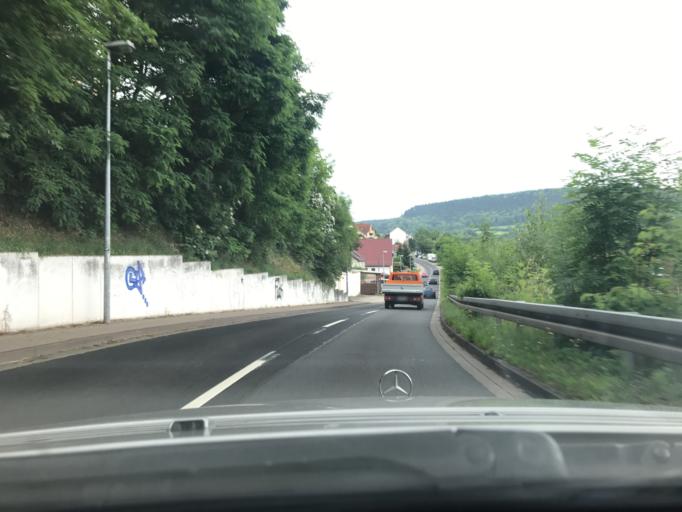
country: DE
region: Thuringia
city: Heilbad Heiligenstadt
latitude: 51.3819
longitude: 10.1361
